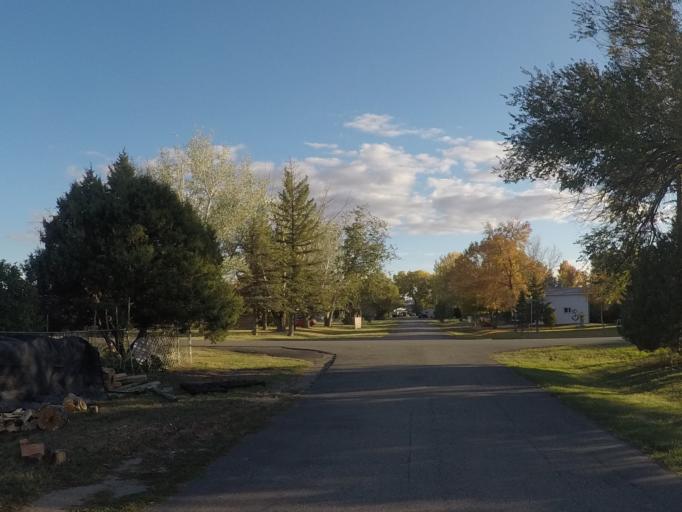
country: US
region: Montana
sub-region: Golden Valley County
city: Ryegate
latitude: 46.2949
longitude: -108.9395
